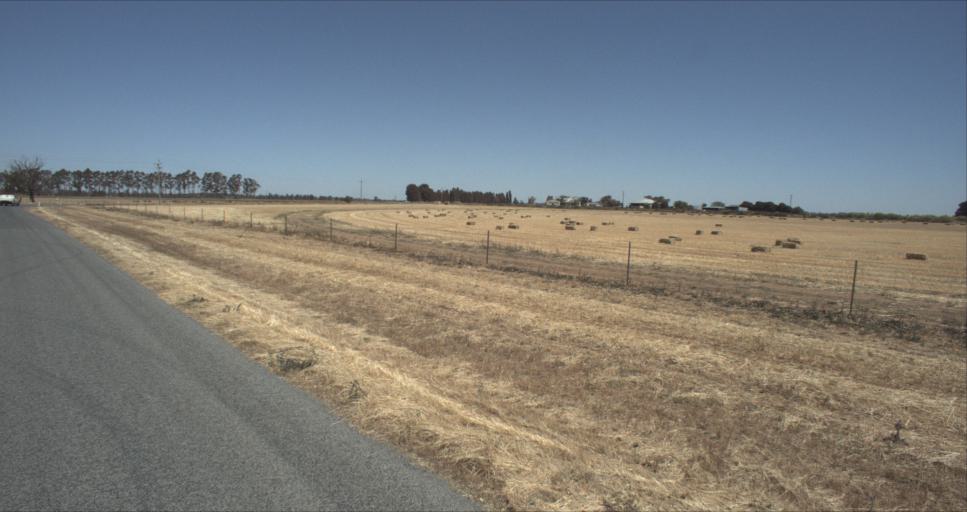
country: AU
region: New South Wales
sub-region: Leeton
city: Leeton
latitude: -34.5325
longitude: 146.4464
